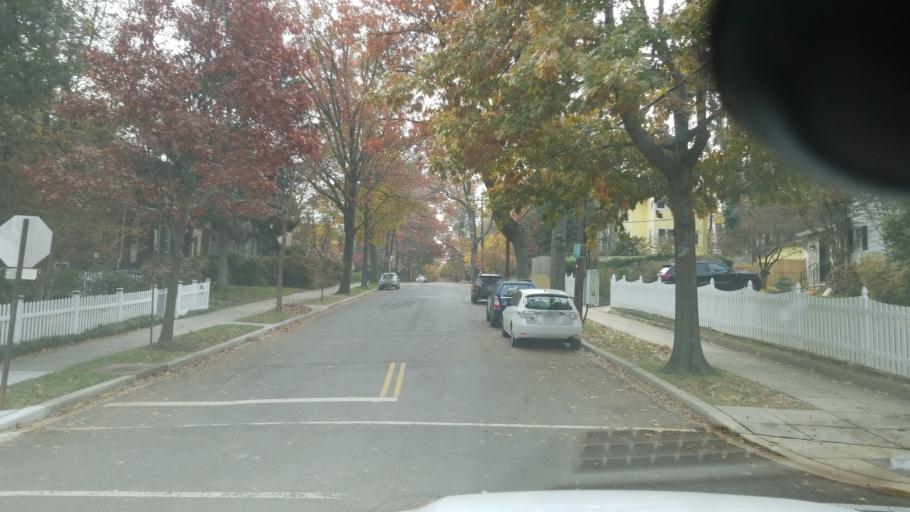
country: US
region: Maryland
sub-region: Montgomery County
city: Friendship Village
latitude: 38.9479
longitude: -77.0746
